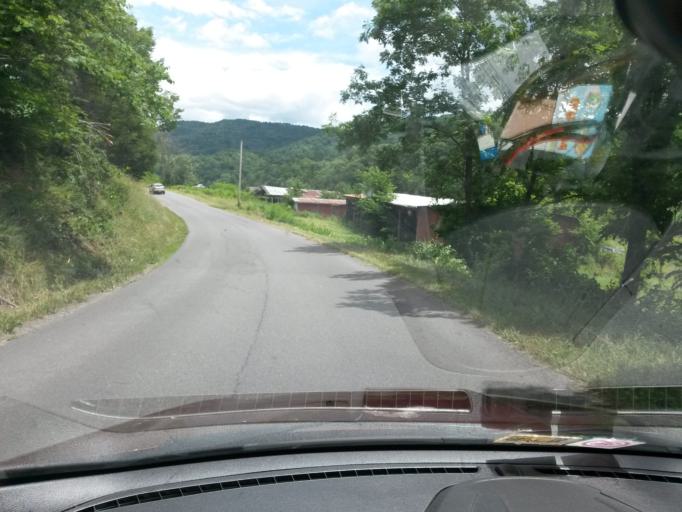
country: US
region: West Virginia
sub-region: Monroe County
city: Union
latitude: 37.4993
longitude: -80.6011
